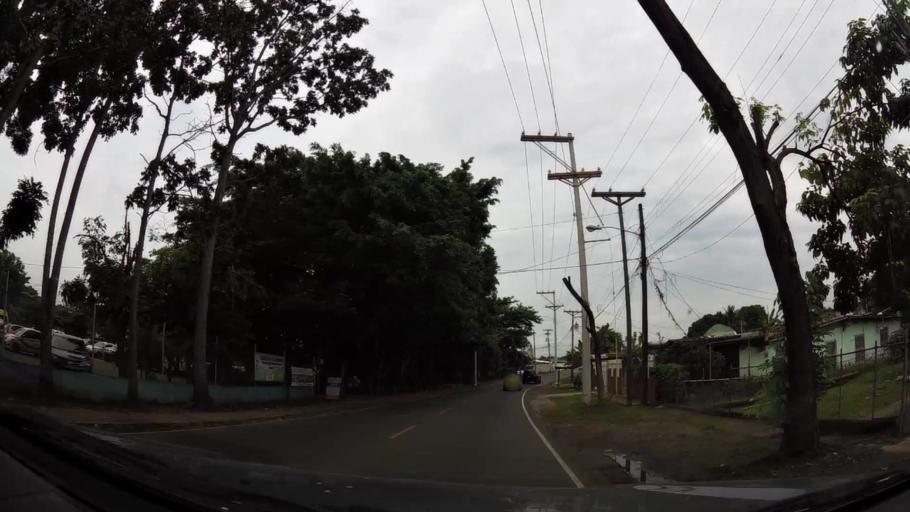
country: PA
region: Panama
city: San Miguelito
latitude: 9.0469
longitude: -79.4347
